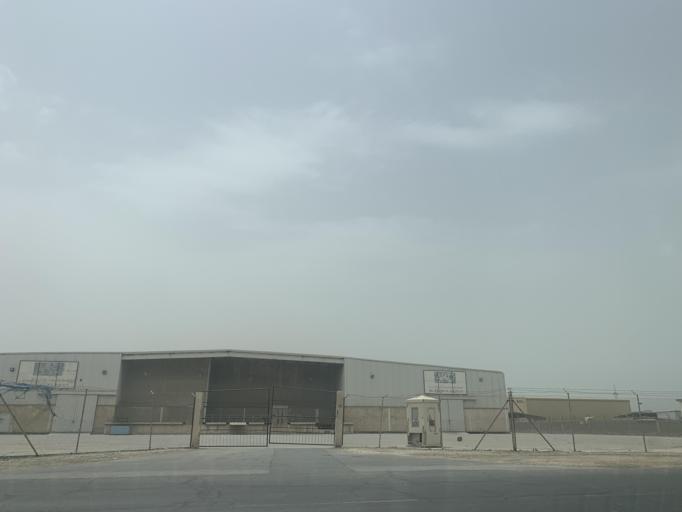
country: BH
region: Northern
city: Sitrah
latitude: 26.1770
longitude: 50.6258
